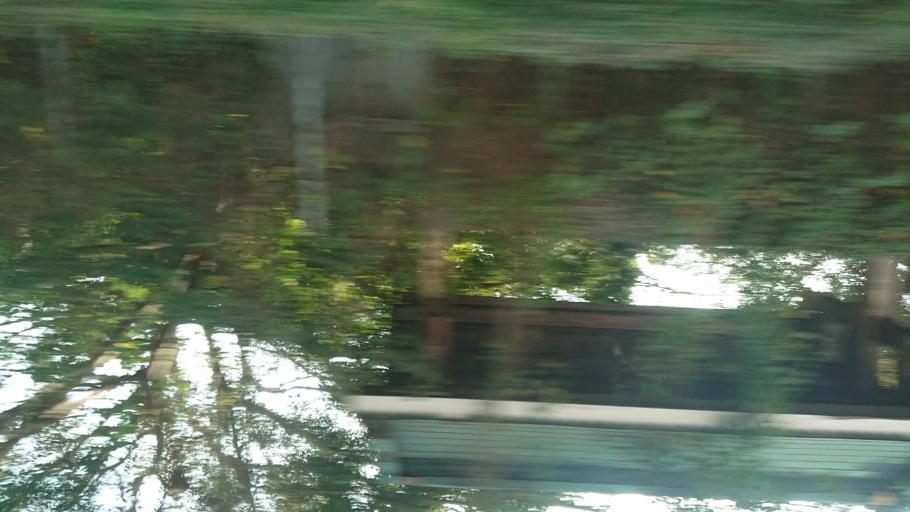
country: TW
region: Taiwan
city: Xinying
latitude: 23.1878
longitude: 120.2718
